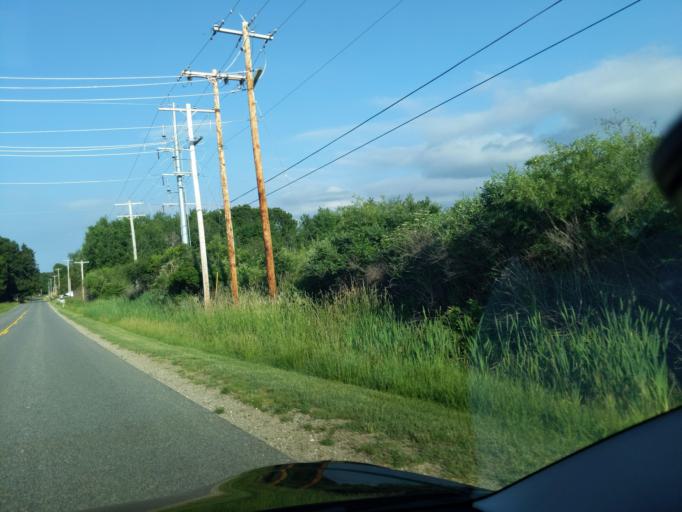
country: US
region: Michigan
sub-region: Muskegon County
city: Whitehall
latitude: 43.4030
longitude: -86.3172
